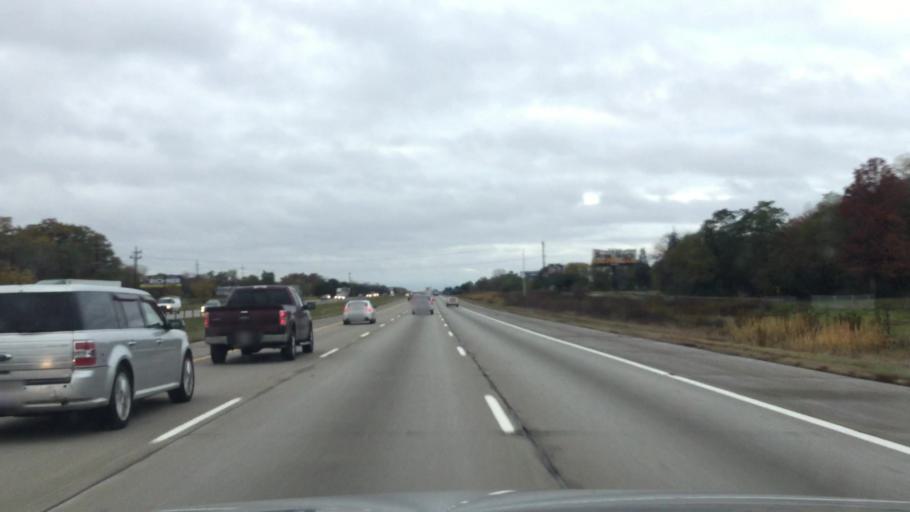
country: US
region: Michigan
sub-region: Wayne County
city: Belleville
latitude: 42.2195
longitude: -83.5011
